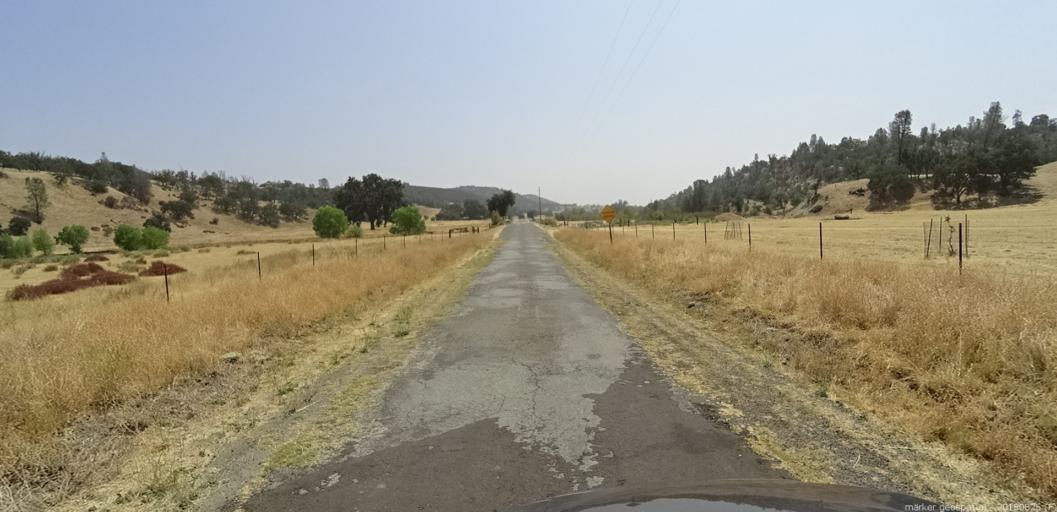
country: US
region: California
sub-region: Fresno County
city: Coalinga
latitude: 35.9471
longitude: -120.4708
